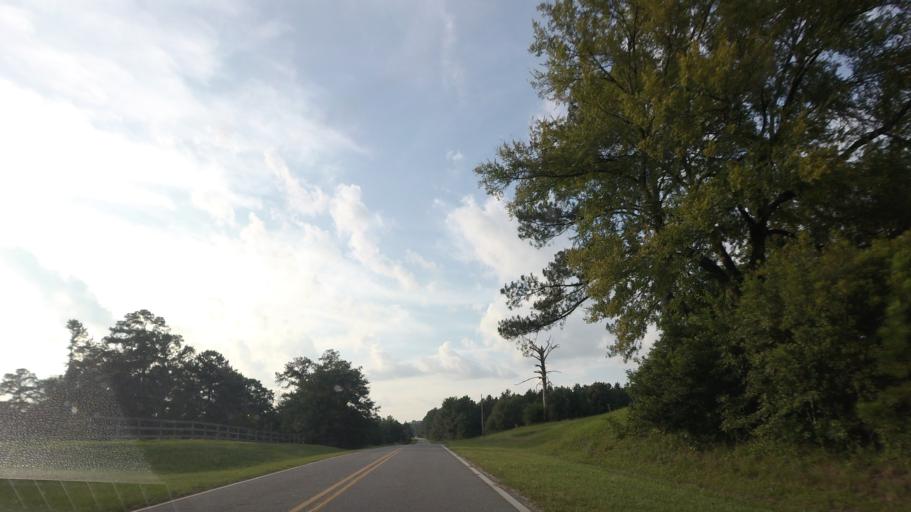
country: US
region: Georgia
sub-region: Wilkinson County
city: Gordon
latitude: 32.8431
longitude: -83.4165
